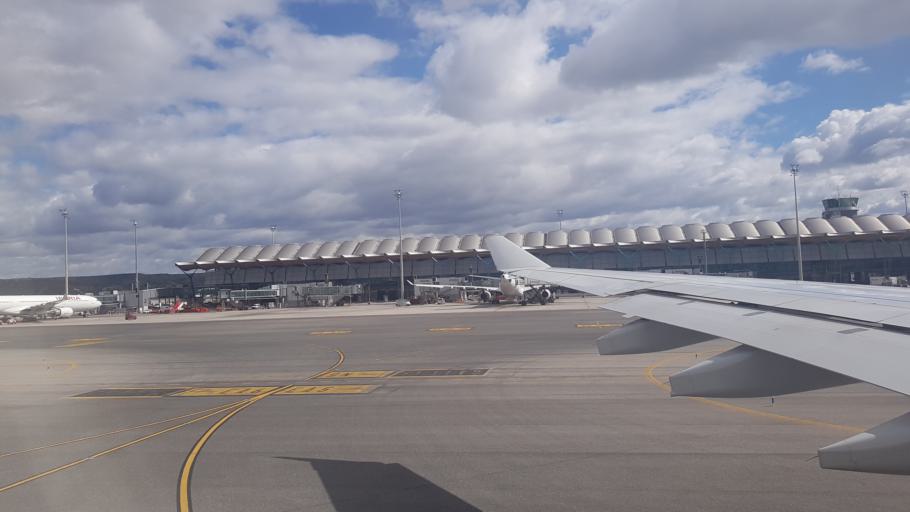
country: ES
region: Madrid
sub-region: Provincia de Madrid
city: Barajas de Madrid
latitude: 40.4973
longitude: -3.5712
